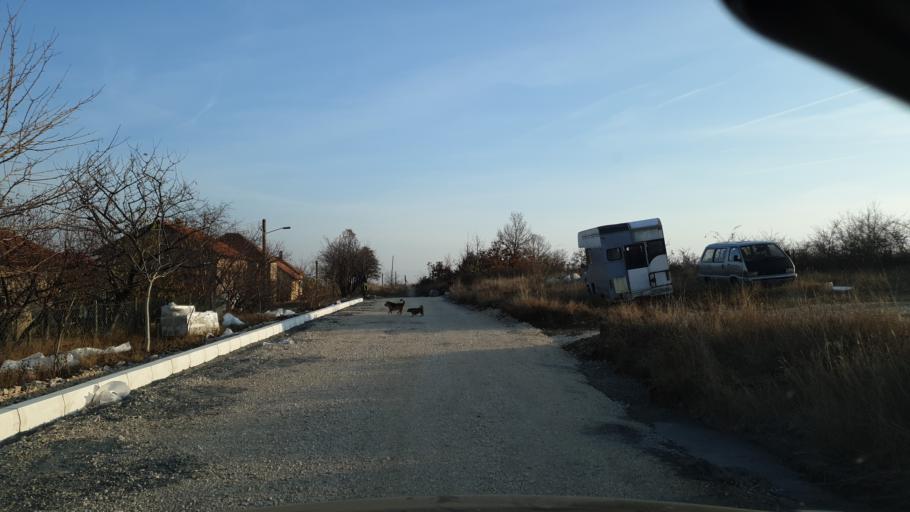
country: RS
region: Central Serbia
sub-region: Borski Okrug
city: Bor
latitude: 44.0540
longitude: 22.0857
